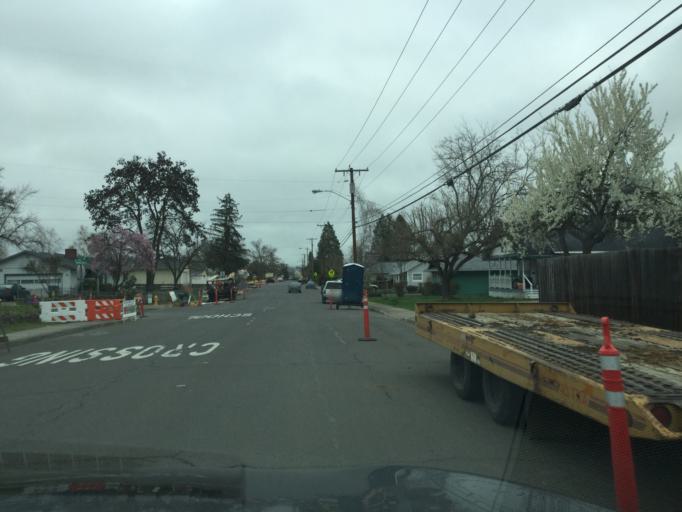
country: US
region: Oregon
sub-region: Jackson County
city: Central Point
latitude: 42.3819
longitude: -122.9197
